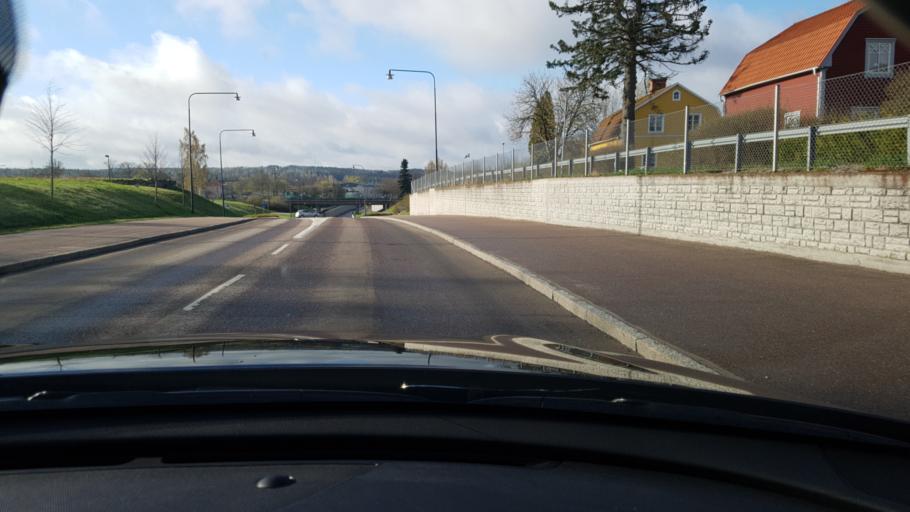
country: SE
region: Vaestmanland
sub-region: Arboga Kommun
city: Arboga
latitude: 59.3994
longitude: 15.8321
